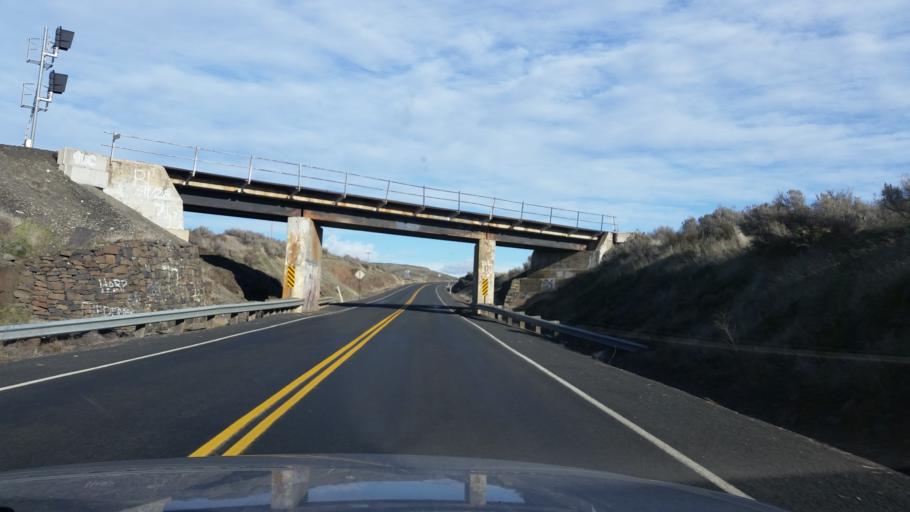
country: US
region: Washington
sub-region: Adams County
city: Ritzville
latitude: 47.3332
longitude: -118.6592
